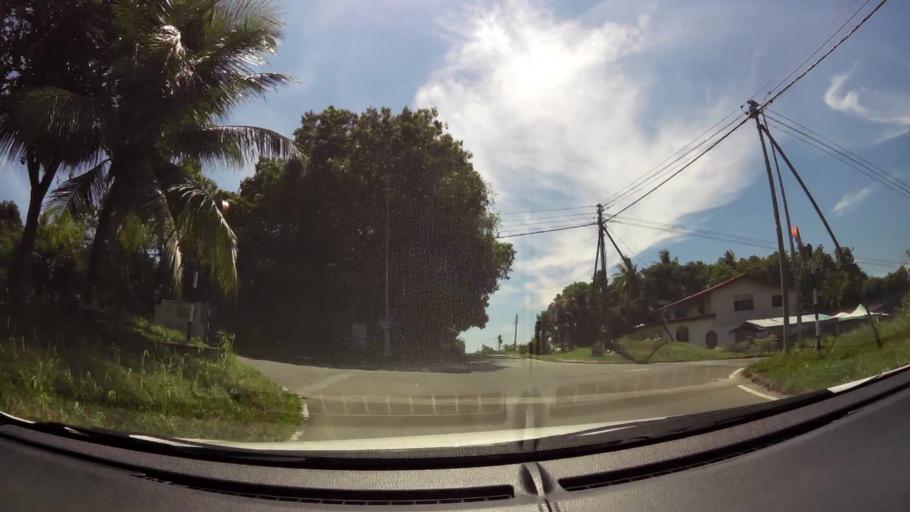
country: BN
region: Brunei and Muara
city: Bandar Seri Begawan
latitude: 4.9412
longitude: 114.9493
